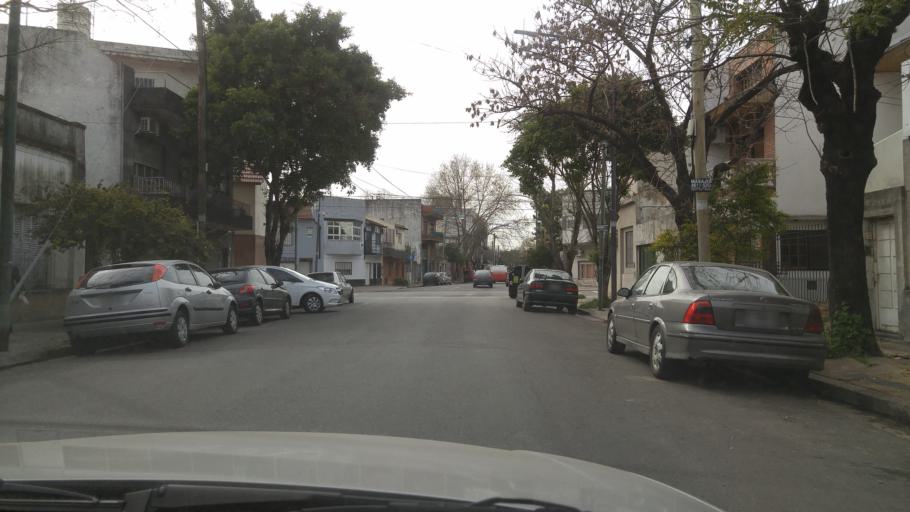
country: AR
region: Buenos Aires F.D.
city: Villa Santa Rita
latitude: -34.6311
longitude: -58.4953
